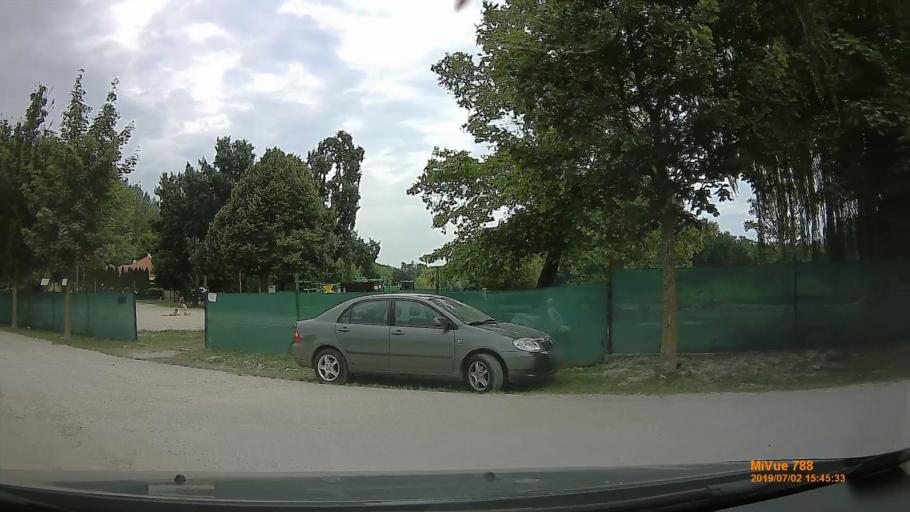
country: HU
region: Gyor-Moson-Sopron
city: Mosonmagyarovar
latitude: 47.8745
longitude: 17.2909
